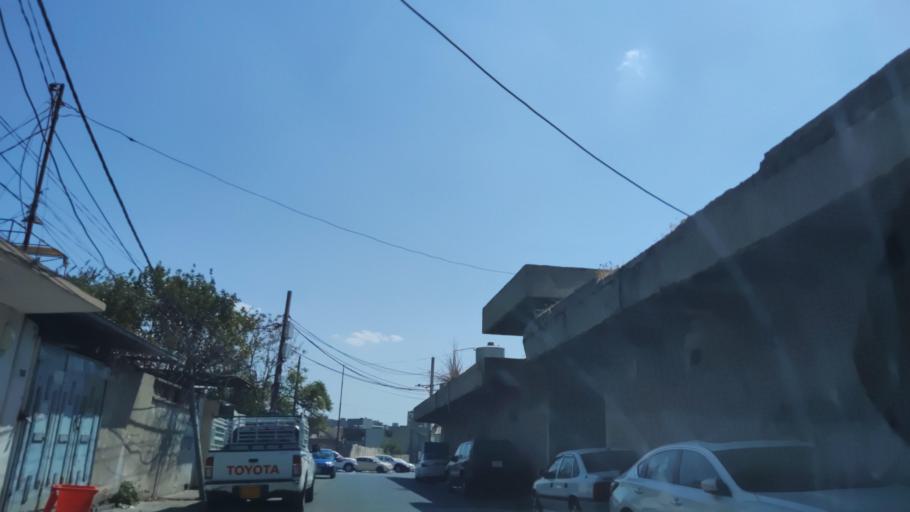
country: IQ
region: Arbil
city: Erbil
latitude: 36.1869
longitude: 44.0211
